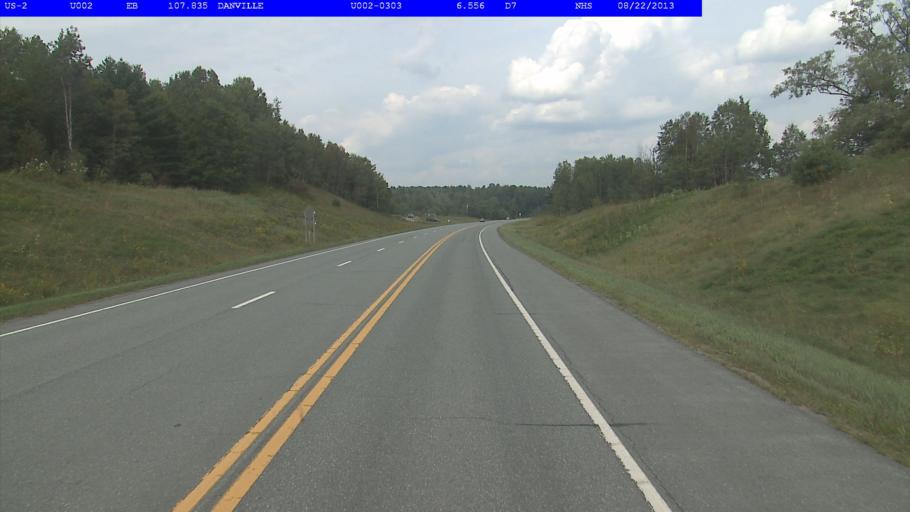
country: US
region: Vermont
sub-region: Caledonia County
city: St Johnsbury
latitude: 44.4284
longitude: -72.1055
